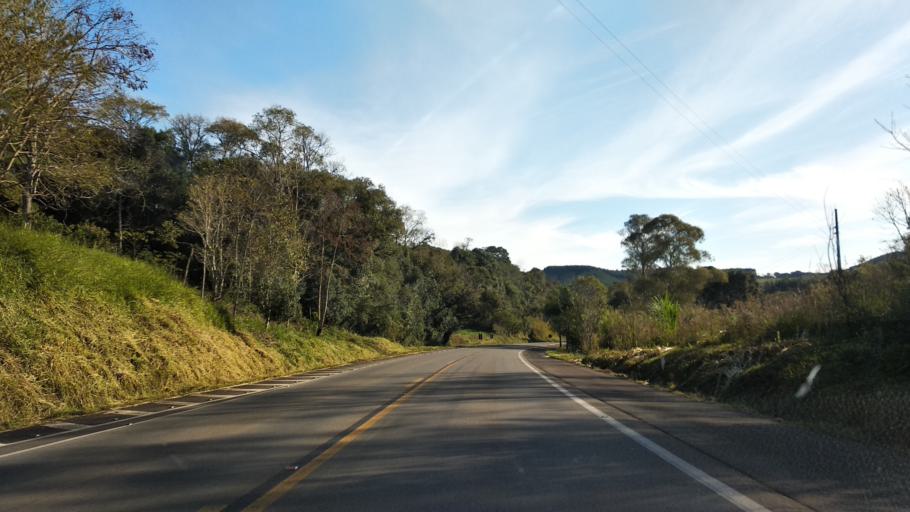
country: BR
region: Santa Catarina
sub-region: Celso Ramos
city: Celso Ramos
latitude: -27.5488
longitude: -51.4368
